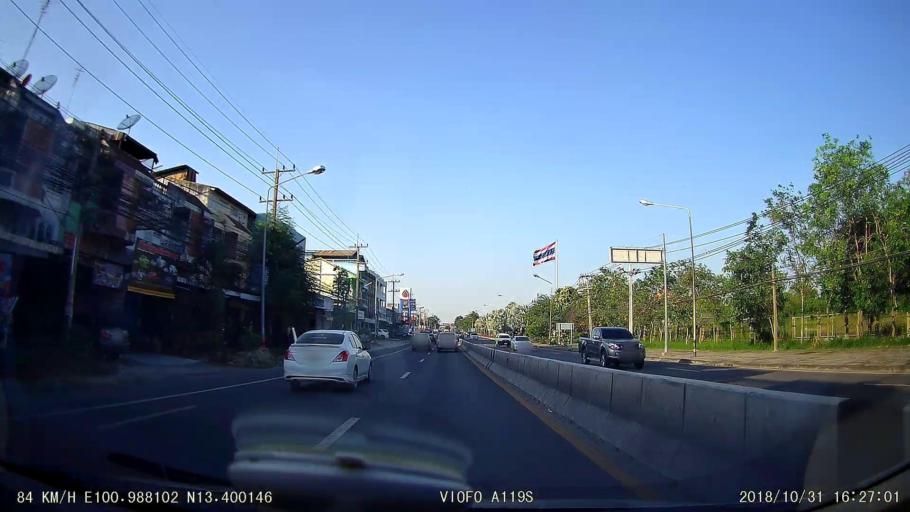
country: TH
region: Chon Buri
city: Chon Buri
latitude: 13.4005
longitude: 100.9881
